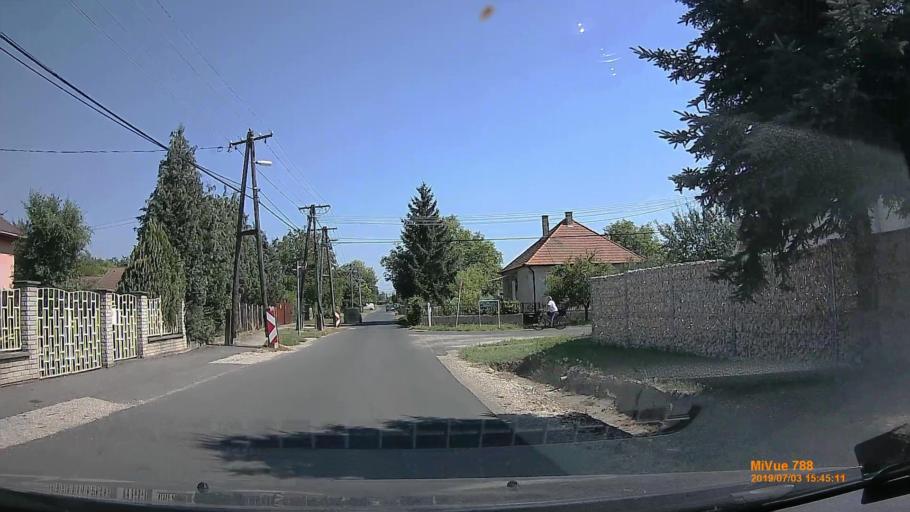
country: HU
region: Gyor-Moson-Sopron
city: Toltestava
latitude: 47.6942
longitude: 17.7594
